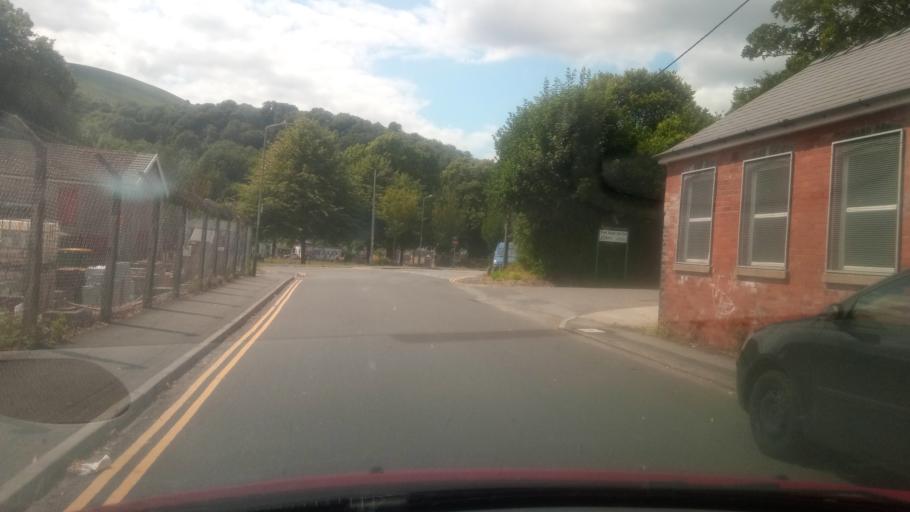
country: GB
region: Wales
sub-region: Caerphilly County Borough
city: Risca
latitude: 51.6077
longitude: -3.0983
